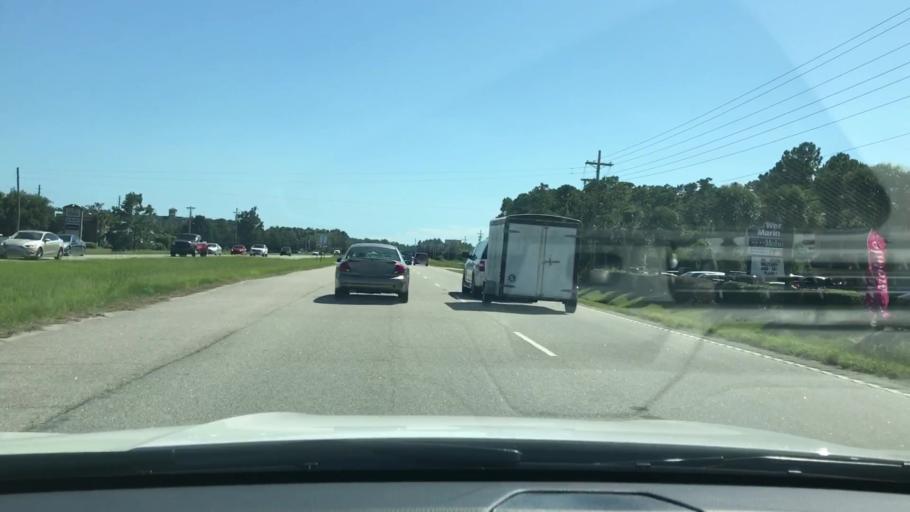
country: US
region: South Carolina
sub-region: Horry County
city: Garden City
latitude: 33.5808
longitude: -79.0283
